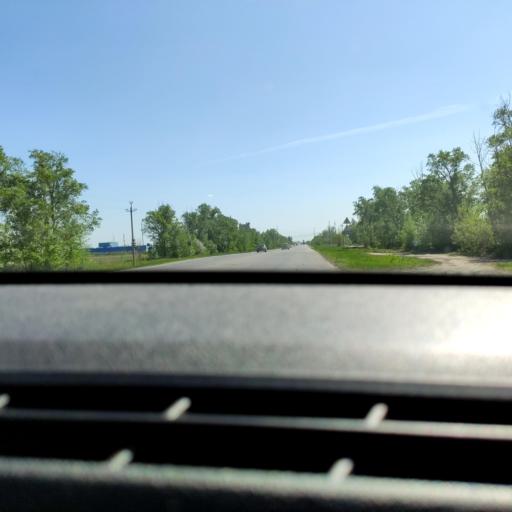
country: RU
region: Samara
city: Tol'yatti
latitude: 53.5908
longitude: 49.4062
